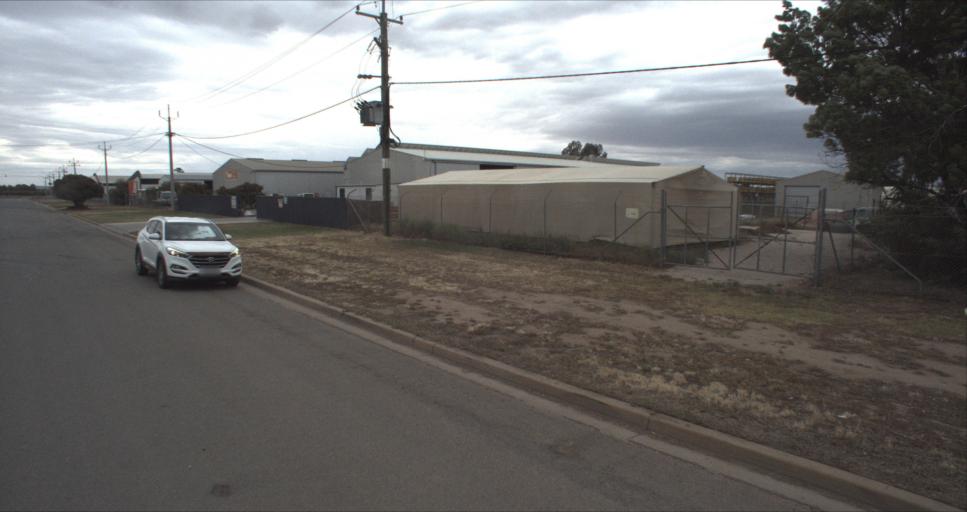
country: AU
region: New South Wales
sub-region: Leeton
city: Leeton
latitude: -34.5484
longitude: 146.3907
